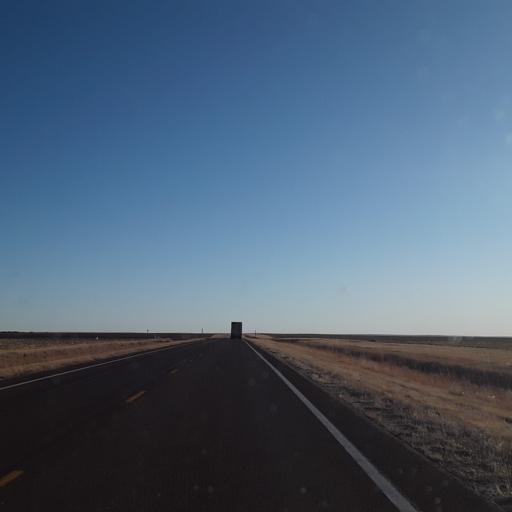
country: US
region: Kansas
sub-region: Sherman County
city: Goodland
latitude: 39.1503
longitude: -101.7267
